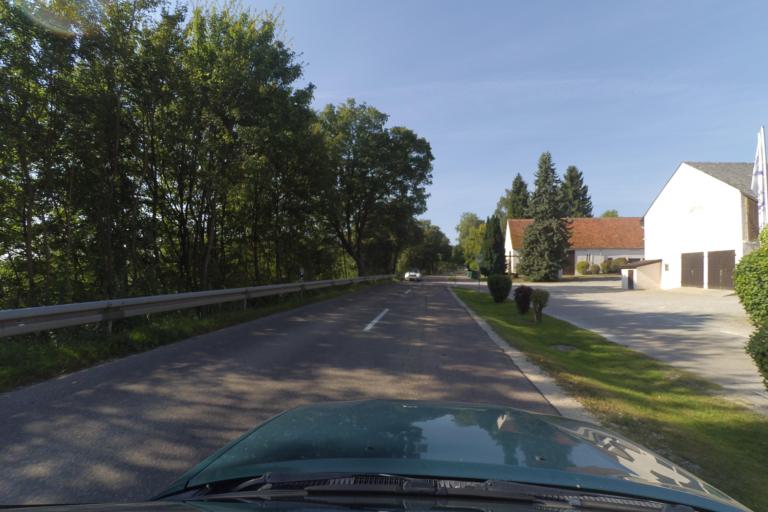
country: DE
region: Bavaria
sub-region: Swabia
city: Genderkingen
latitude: 48.7191
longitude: 10.8484
